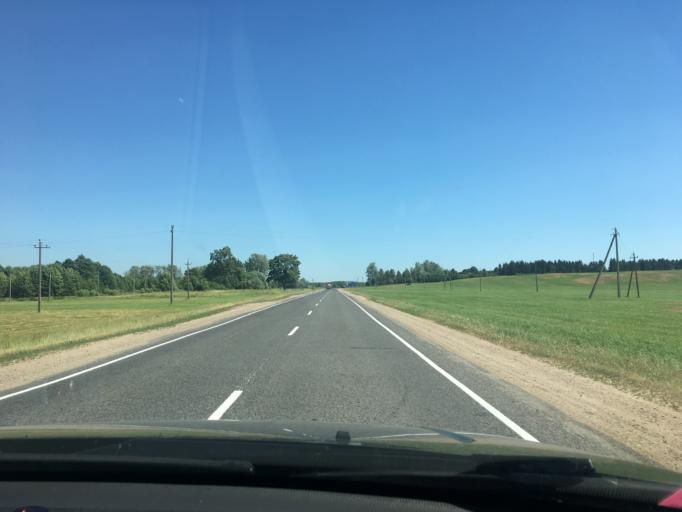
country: BY
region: Grodnenskaya
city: Hal'shany
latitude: 54.2562
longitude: 25.9994
